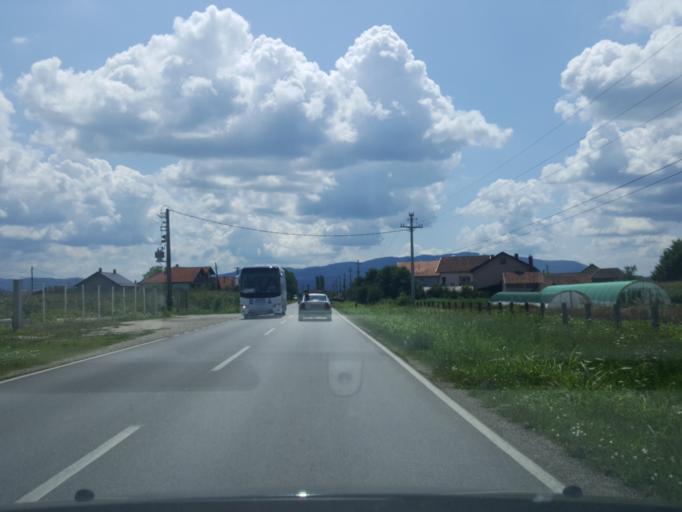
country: RS
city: Lipnicki Sor
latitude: 44.5727
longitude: 19.2418
